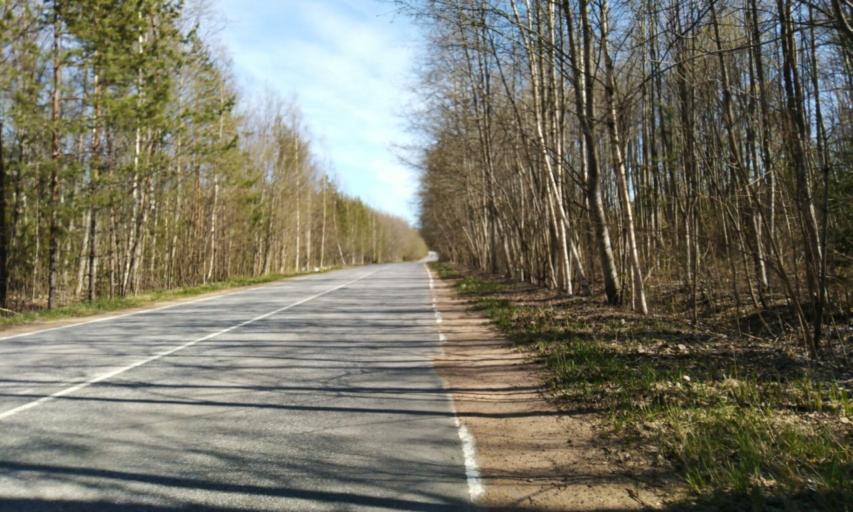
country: RU
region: Leningrad
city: Garbolovo
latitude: 60.4184
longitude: 30.4595
